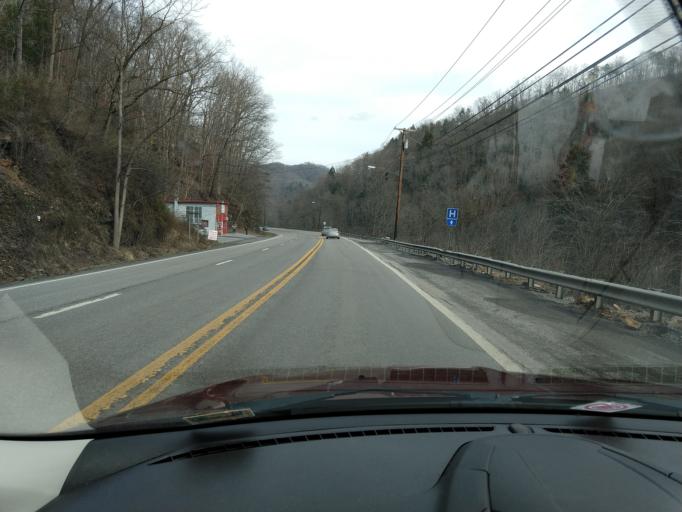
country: US
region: West Virginia
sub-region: McDowell County
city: Welch
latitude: 37.4129
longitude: -81.6046
